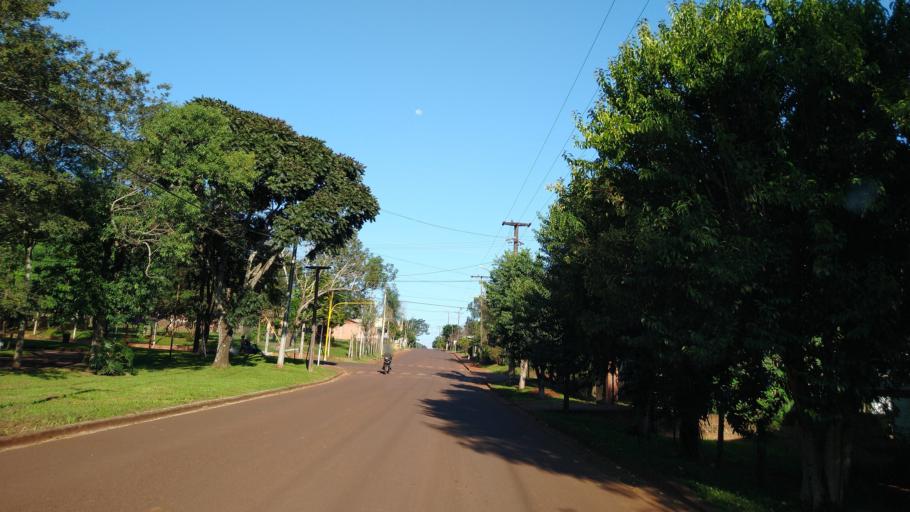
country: AR
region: Misiones
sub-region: Departamento de Montecarlo
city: Montecarlo
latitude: -26.5650
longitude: -54.7534
